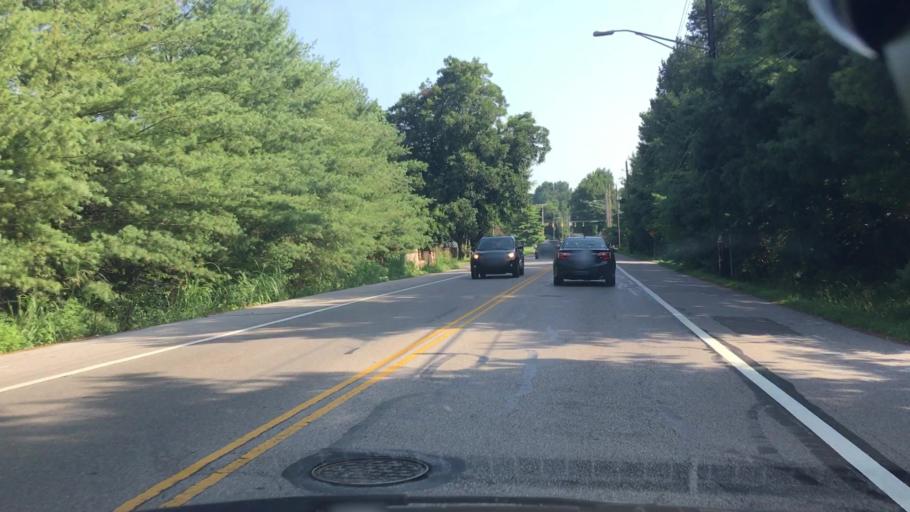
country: US
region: Indiana
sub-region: Vanderburgh County
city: Melody Hill
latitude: 37.9717
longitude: -87.4744
